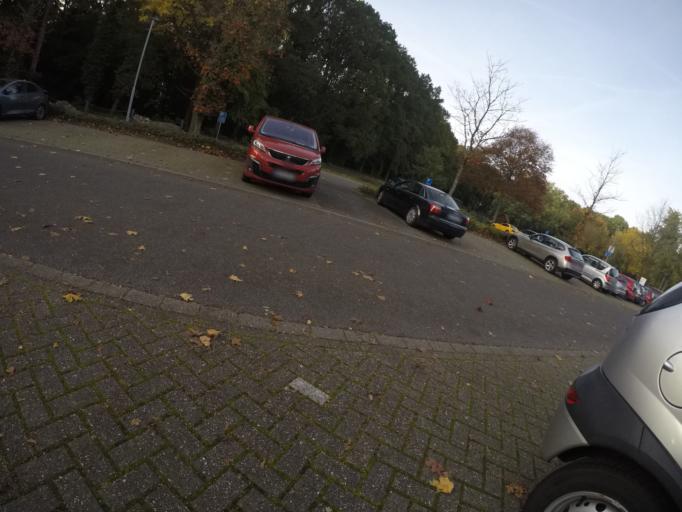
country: DE
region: North Rhine-Westphalia
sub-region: Regierungsbezirk Munster
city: Rhede
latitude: 51.8398
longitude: 6.6908
